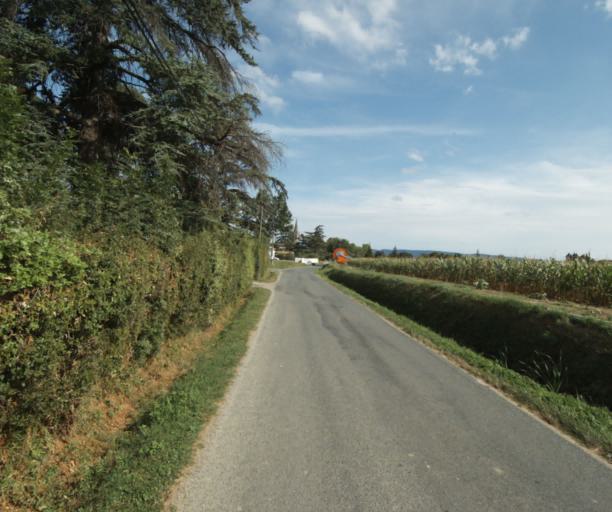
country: FR
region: Midi-Pyrenees
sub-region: Departement du Tarn
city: Puylaurens
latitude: 43.5250
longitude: 1.9819
